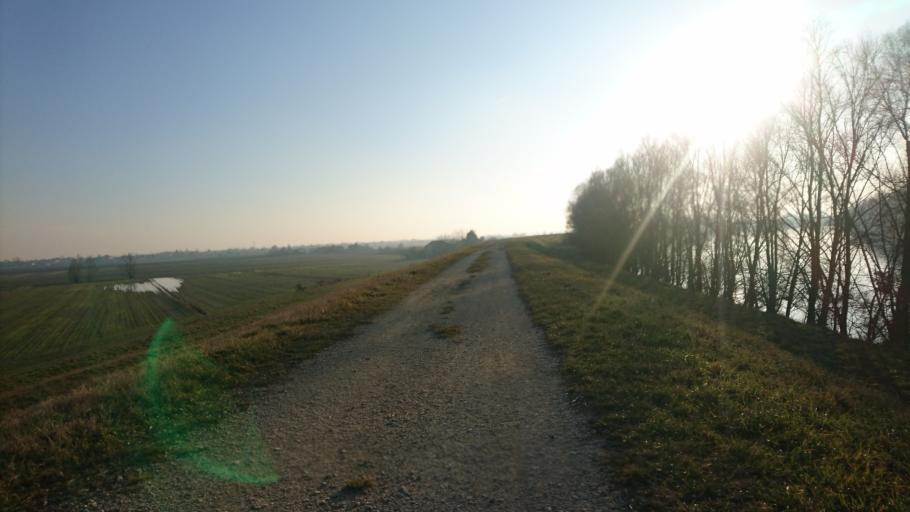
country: IT
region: Veneto
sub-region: Provincia di Rovigo
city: Mardimago
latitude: 45.1264
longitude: 11.8383
